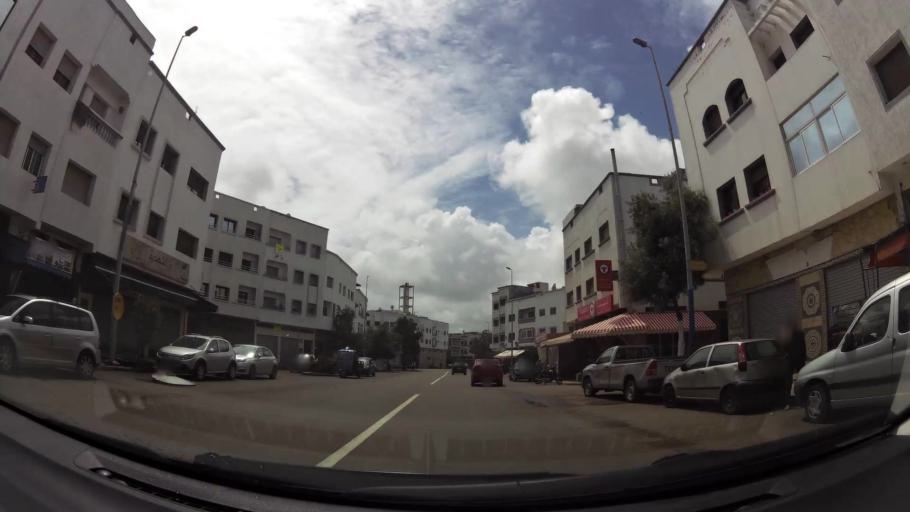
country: MA
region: Grand Casablanca
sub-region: Casablanca
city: Casablanca
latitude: 33.5465
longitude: -7.6819
